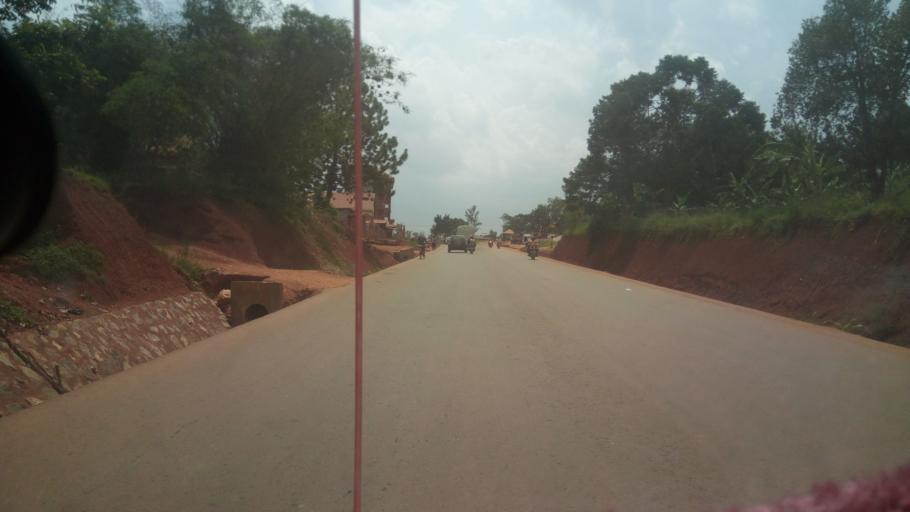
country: UG
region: Central Region
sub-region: Wakiso District
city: Wakiso
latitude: 0.3948
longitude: 32.4993
